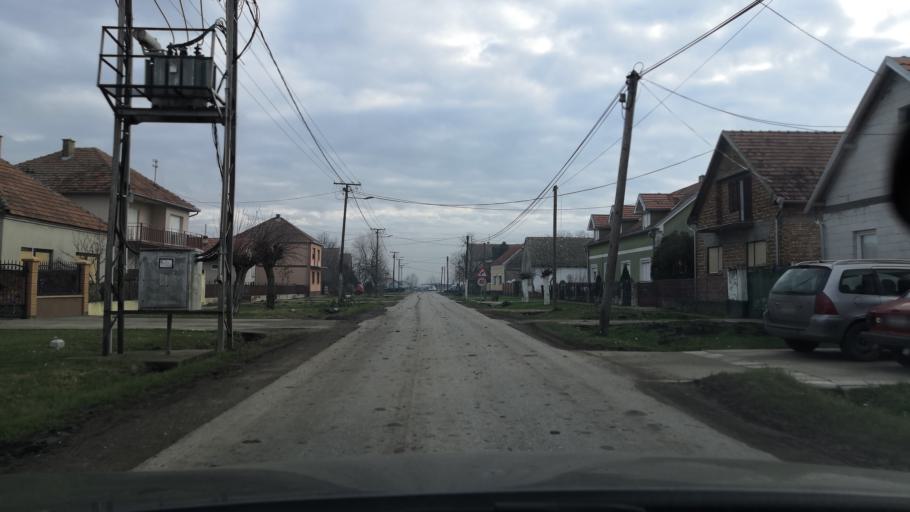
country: RS
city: Ugrinovci
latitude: 44.8878
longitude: 20.1439
